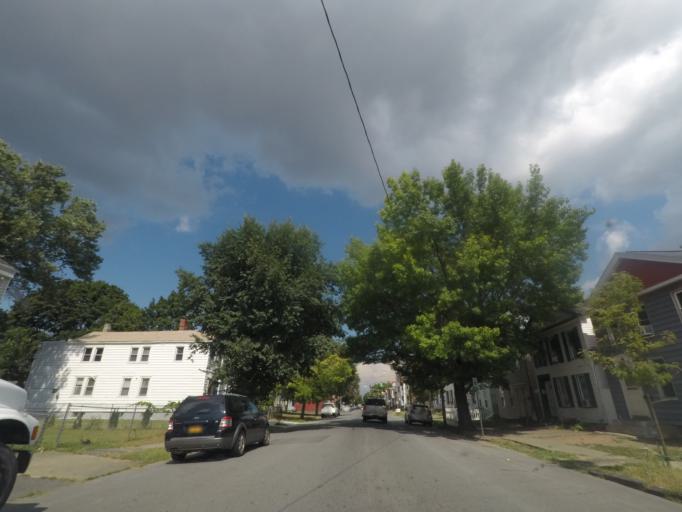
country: US
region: New York
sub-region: Rensselaer County
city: Troy
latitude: 42.7178
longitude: -73.6920
